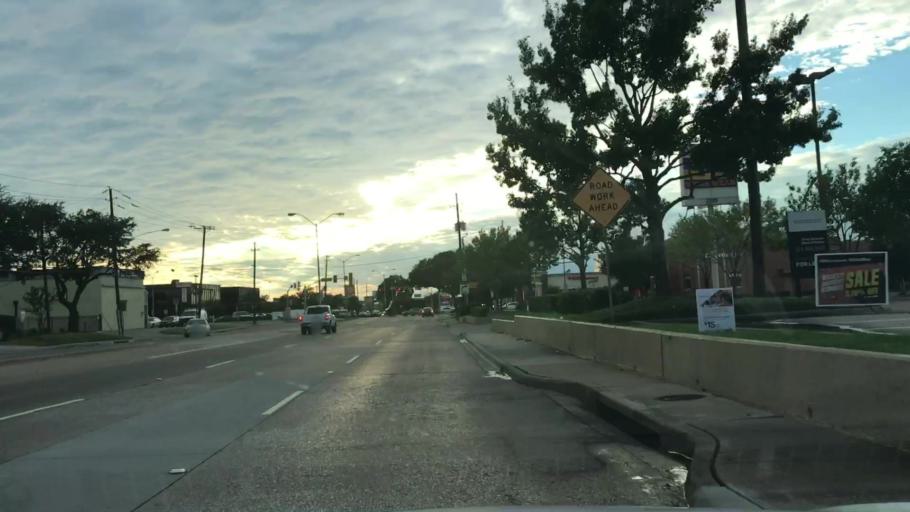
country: US
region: Texas
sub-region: Dallas County
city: Farmers Branch
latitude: 32.9096
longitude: -96.8798
